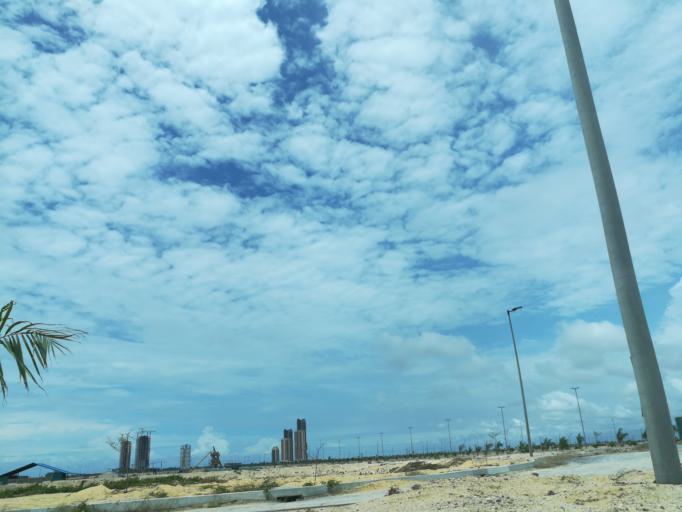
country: NG
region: Lagos
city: Ikoyi
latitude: 6.4115
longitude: 3.4260
